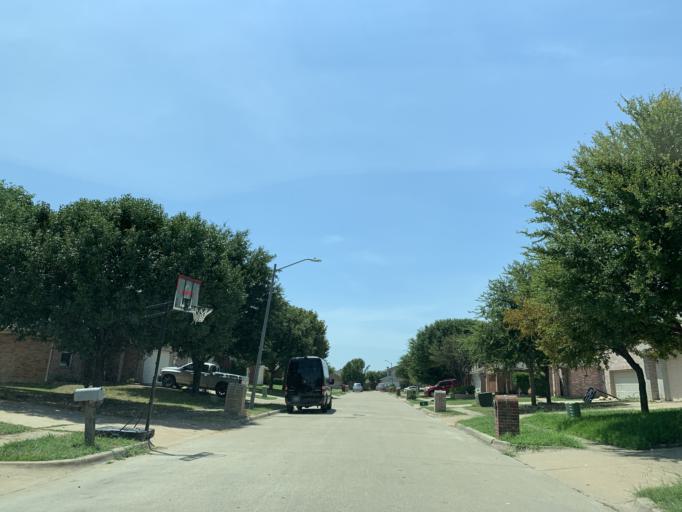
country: US
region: Texas
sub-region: Dallas County
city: Cedar Hill
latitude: 32.6417
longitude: -97.0369
